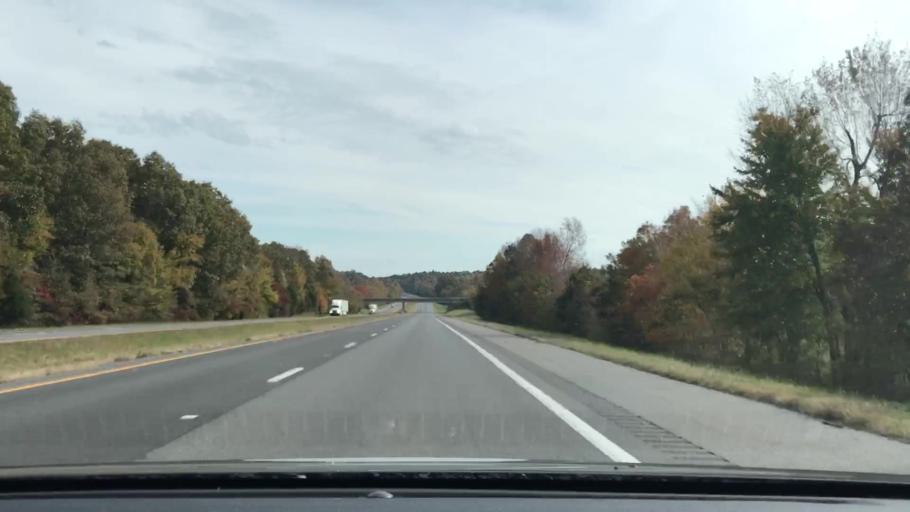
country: US
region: Kentucky
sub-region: Graves County
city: Mayfield
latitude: 36.7879
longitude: -88.5366
